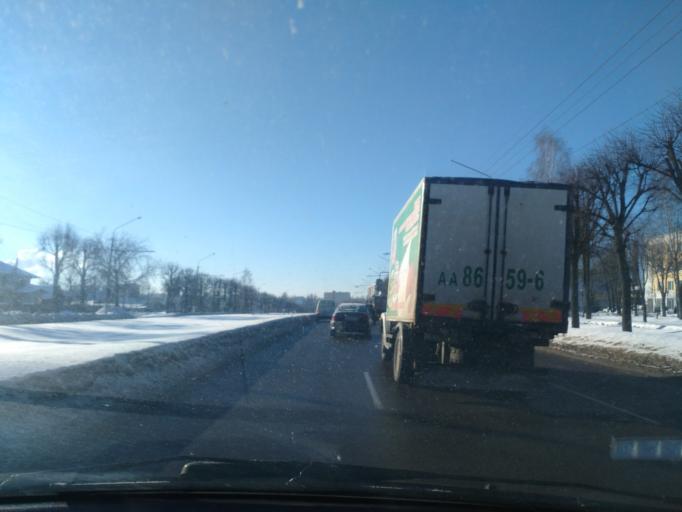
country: BY
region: Mogilev
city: Mahilyow
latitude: 53.9038
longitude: 30.3031
